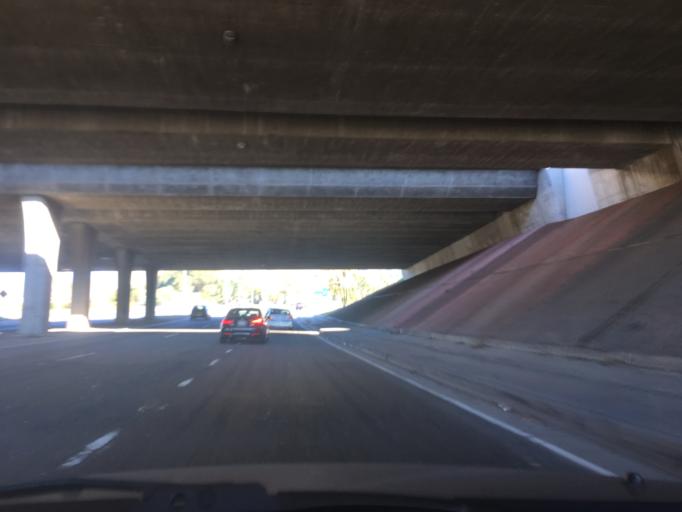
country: US
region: California
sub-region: Santa Clara County
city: Milpitas
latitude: 37.4952
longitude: -121.9235
